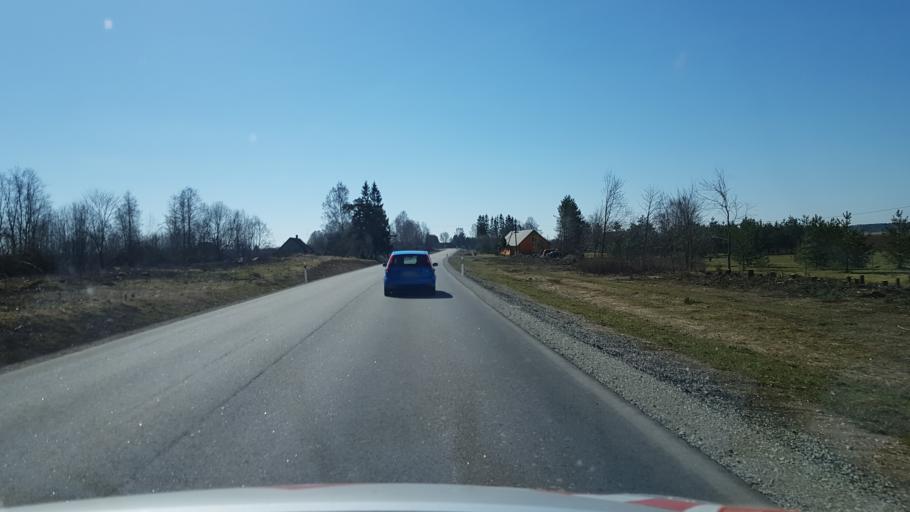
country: EE
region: Laeaene-Virumaa
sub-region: Vinni vald
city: Vinni
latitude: 59.1092
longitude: 26.6184
